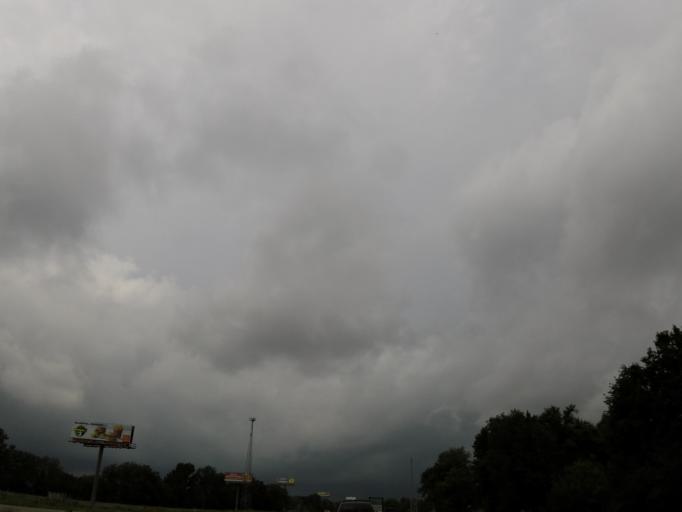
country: US
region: Illinois
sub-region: Jefferson County
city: Ina
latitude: 38.1977
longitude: -88.9078
